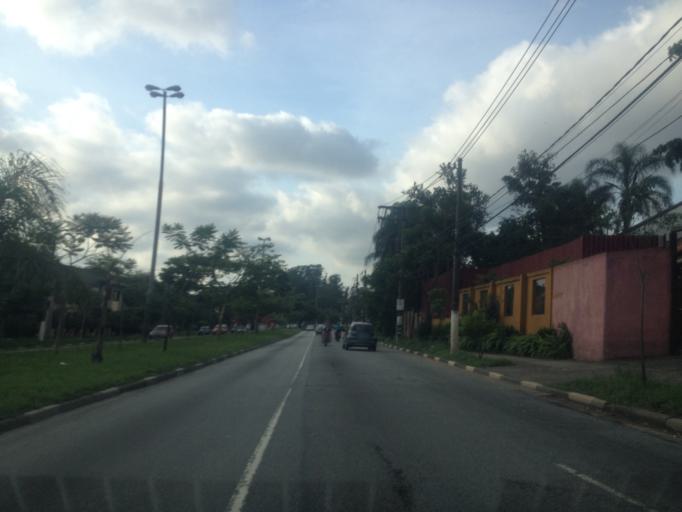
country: BR
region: Sao Paulo
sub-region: Diadema
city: Diadema
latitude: -23.7052
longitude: -46.7138
